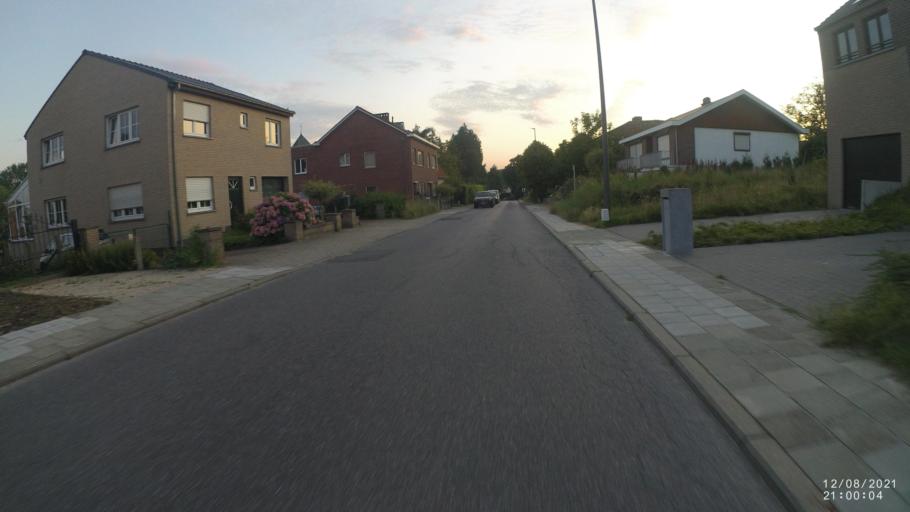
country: BE
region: Flanders
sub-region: Provincie Vlaams-Brabant
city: Dilbeek
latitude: 50.8711
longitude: 4.2477
